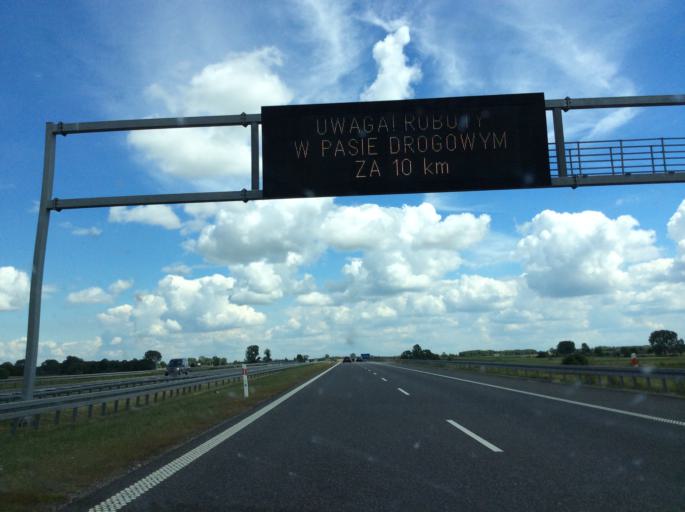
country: PL
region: Lodz Voivodeship
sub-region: Powiat poddebicki
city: Wartkowice
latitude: 51.9981
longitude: 19.0170
